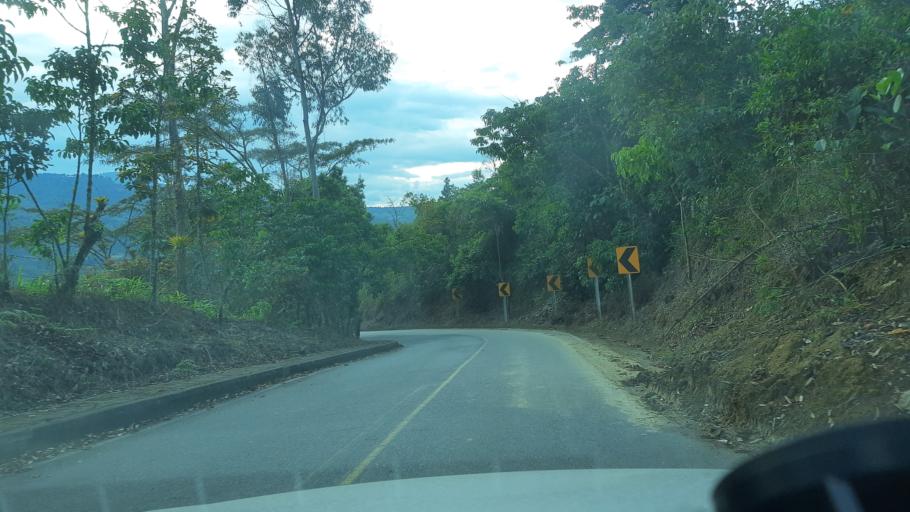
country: CO
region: Boyaca
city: Chivor
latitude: 4.9762
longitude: -73.3289
